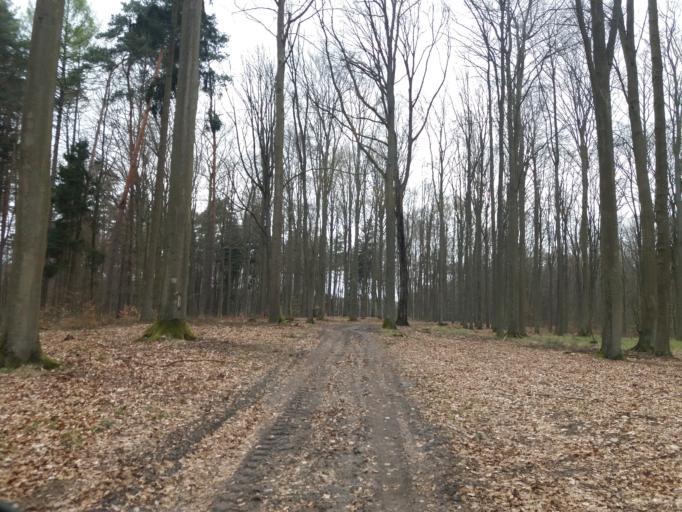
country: PL
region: West Pomeranian Voivodeship
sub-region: Powiat choszczenski
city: Drawno
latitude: 53.1073
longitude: 15.8405
